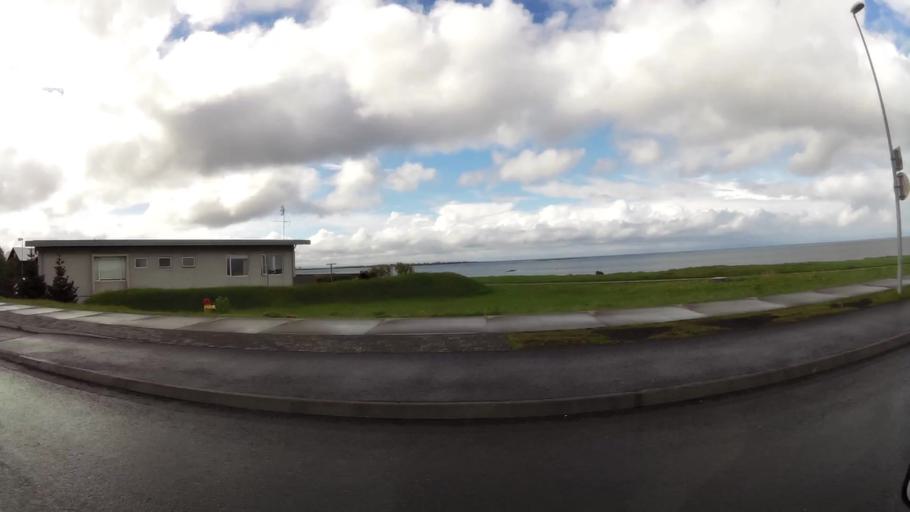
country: IS
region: Capital Region
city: Seltjarnarnes
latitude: 64.1320
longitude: -21.9584
